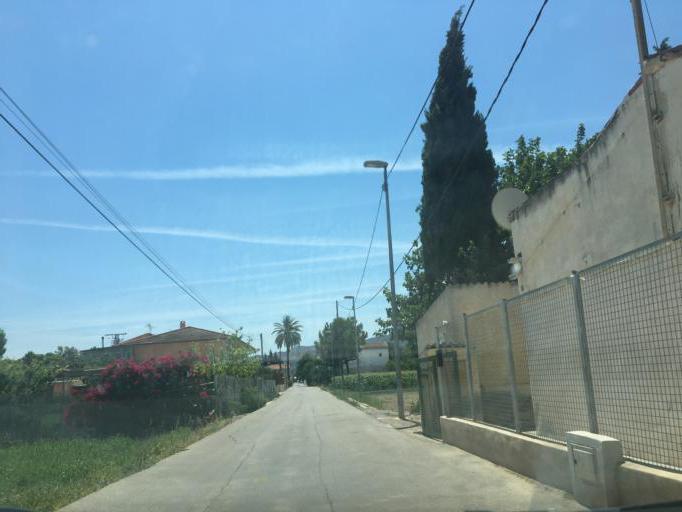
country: ES
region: Murcia
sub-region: Murcia
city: Santomera
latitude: 38.0195
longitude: -1.0564
